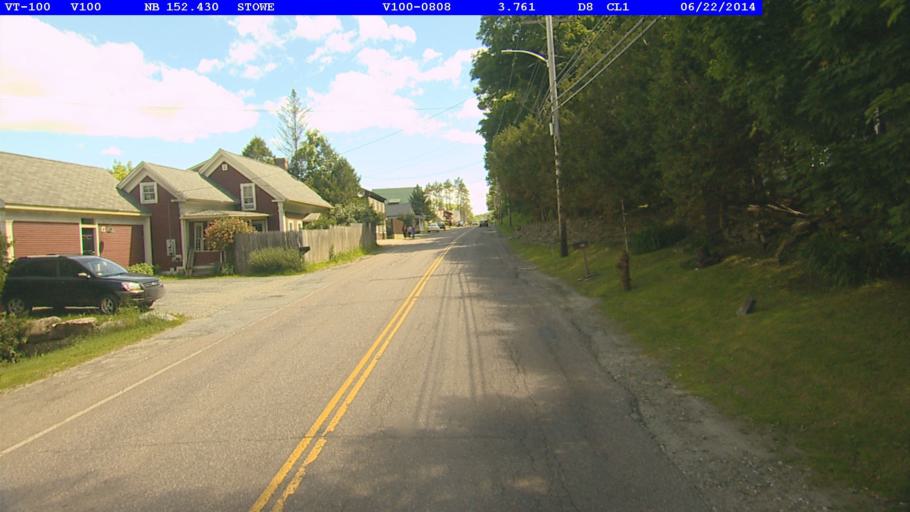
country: US
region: Vermont
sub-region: Lamoille County
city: Morristown
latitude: 44.4678
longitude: -72.6798
